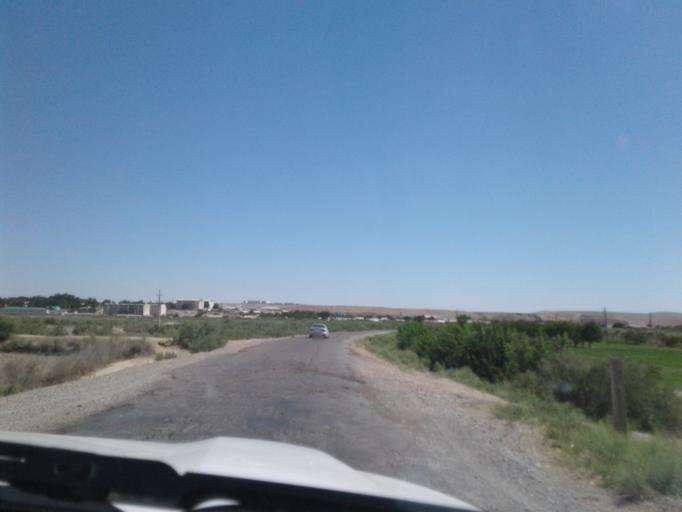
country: AF
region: Badghis
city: Bala Murghab
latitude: 35.9650
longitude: 62.9079
